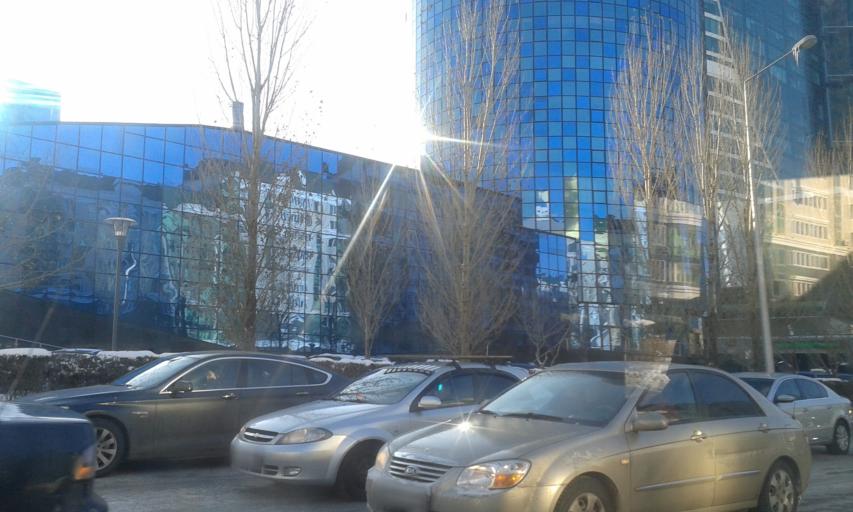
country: KZ
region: Astana Qalasy
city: Astana
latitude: 51.1247
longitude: 71.4373
